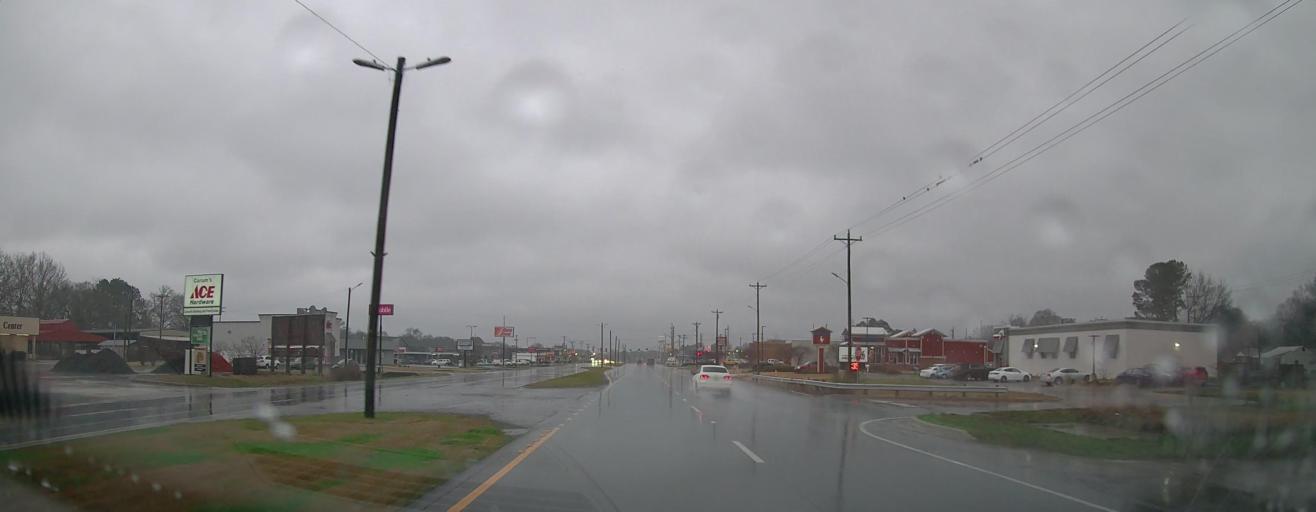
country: US
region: Alabama
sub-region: Morgan County
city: Hartselle
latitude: 34.4452
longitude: -86.9435
